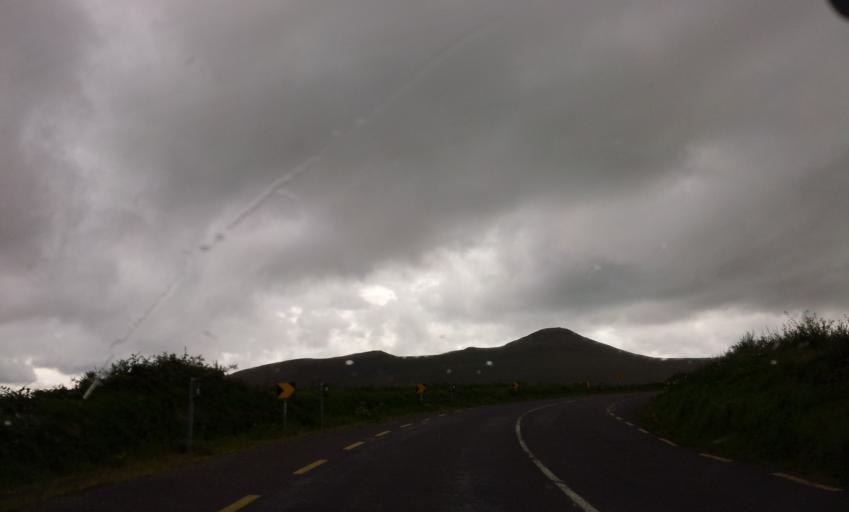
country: IE
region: Munster
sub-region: Ciarrai
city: Killorglin
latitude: 52.1762
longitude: -9.9887
